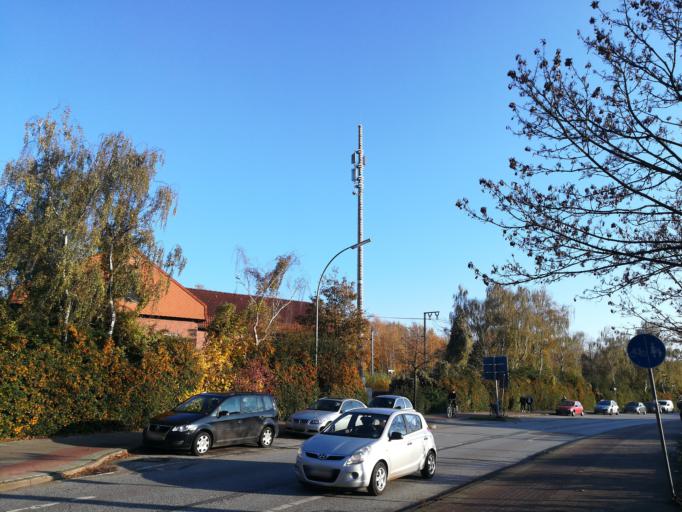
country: DE
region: Schleswig-Holstein
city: Elmshorn
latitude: 53.7525
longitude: 9.6587
